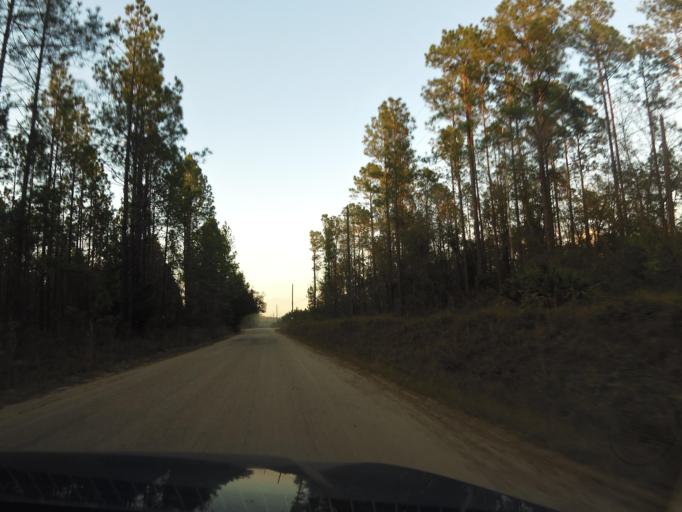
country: US
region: Florida
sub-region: Clay County
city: Green Cove Springs
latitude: 29.8749
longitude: -81.7941
